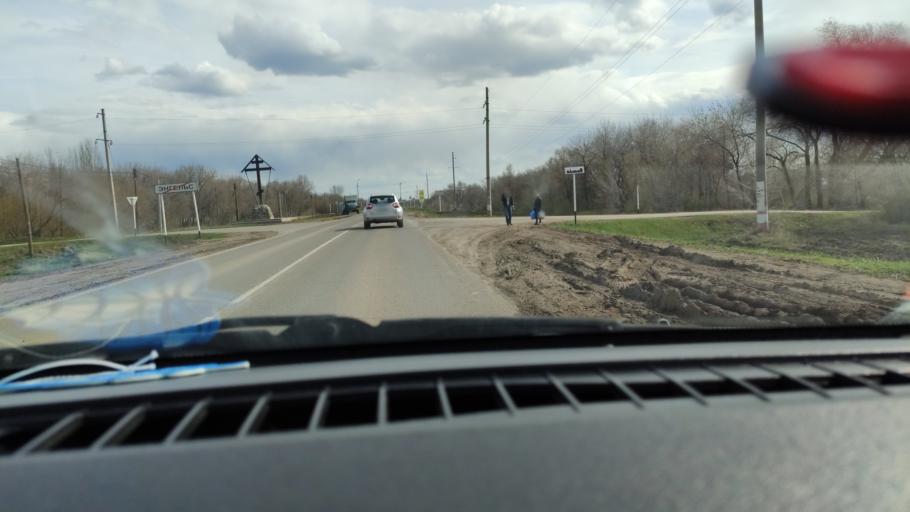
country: RU
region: Saratov
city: Privolzhskiy
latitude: 51.3854
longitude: 46.0398
